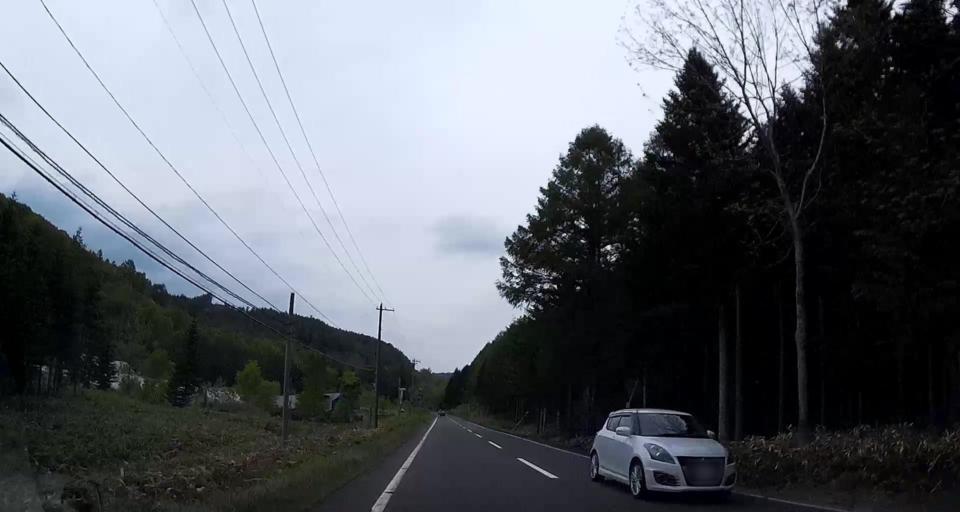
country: JP
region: Hokkaido
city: Shiraoi
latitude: 42.6836
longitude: 141.1016
